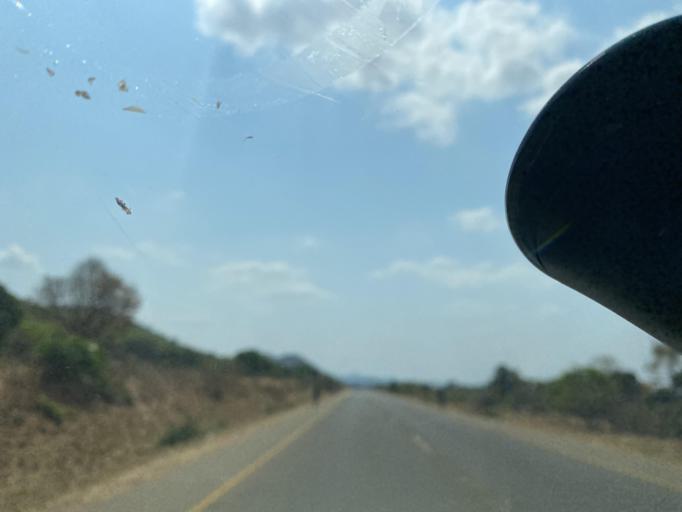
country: ZM
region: Lusaka
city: Chongwe
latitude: -15.6004
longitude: 28.7310
